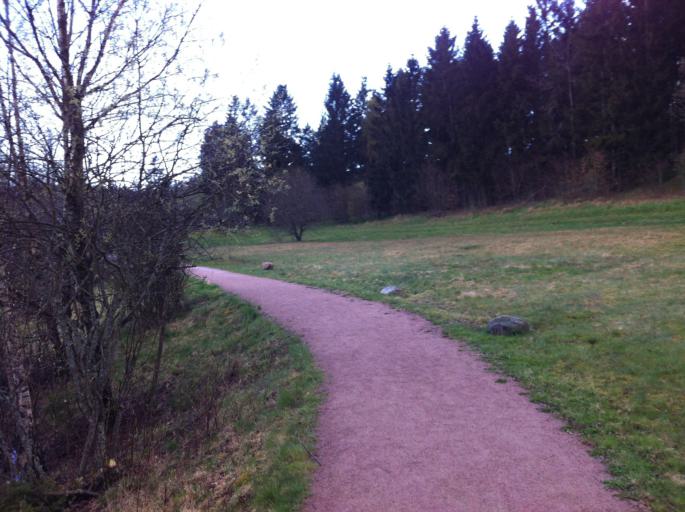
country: SE
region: Skane
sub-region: Horby Kommun
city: Hoerby
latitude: 55.9192
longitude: 13.6283
